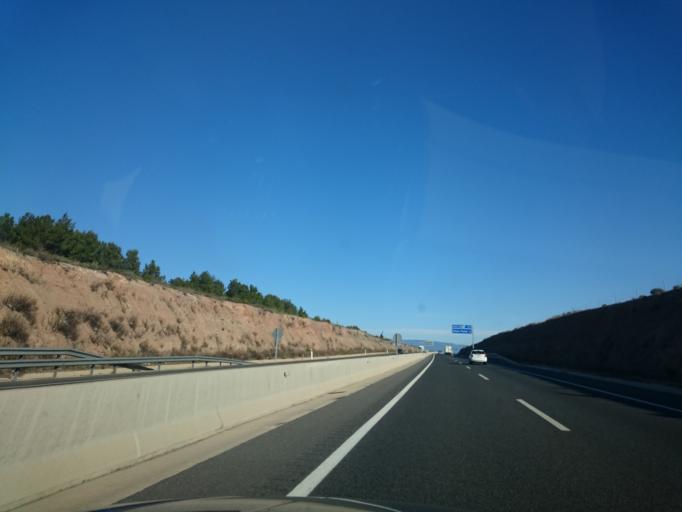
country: ES
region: Catalonia
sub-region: Provincia de Tarragona
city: Colldejou
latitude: 41.0117
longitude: 0.9214
